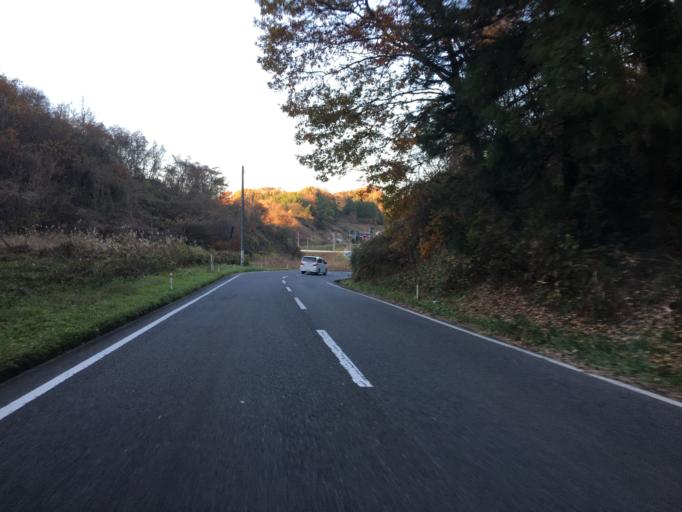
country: JP
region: Fukushima
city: Motomiya
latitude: 37.5253
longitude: 140.4602
